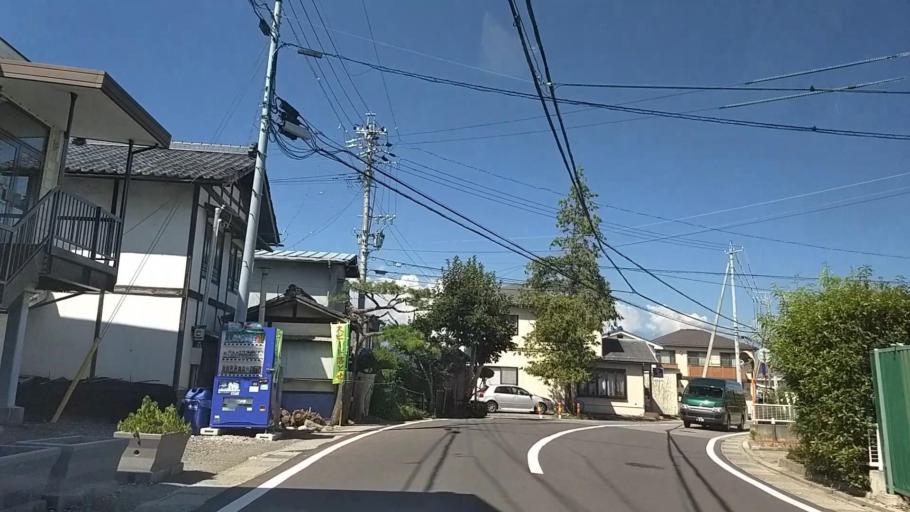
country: JP
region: Nagano
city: Matsumoto
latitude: 36.2362
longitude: 137.9966
